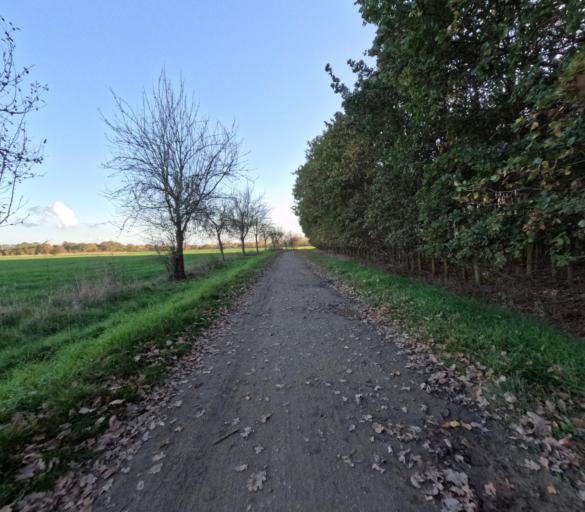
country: DE
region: Saxony-Anhalt
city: Zoschen
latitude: 51.3665
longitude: 12.1080
